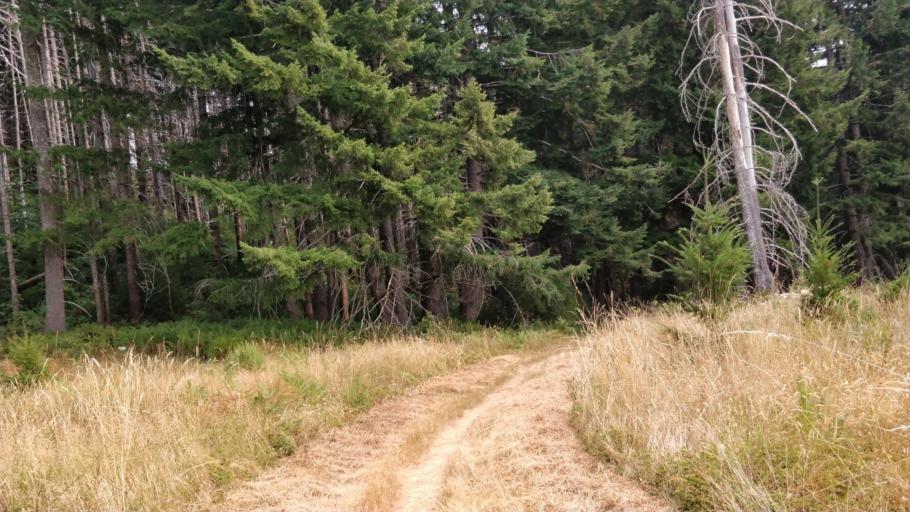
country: US
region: California
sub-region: Humboldt County
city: Westhaven-Moonstone
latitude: 41.2048
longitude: -123.9503
